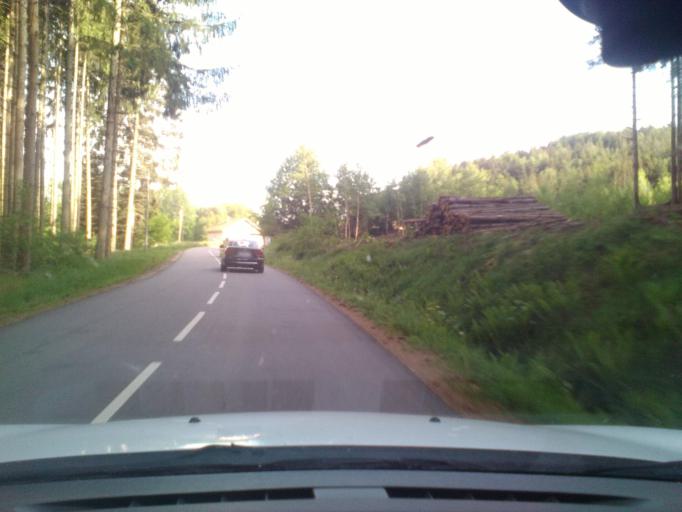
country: FR
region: Lorraine
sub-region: Departement des Vosges
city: Bruyeres
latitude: 48.2440
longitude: 6.7303
